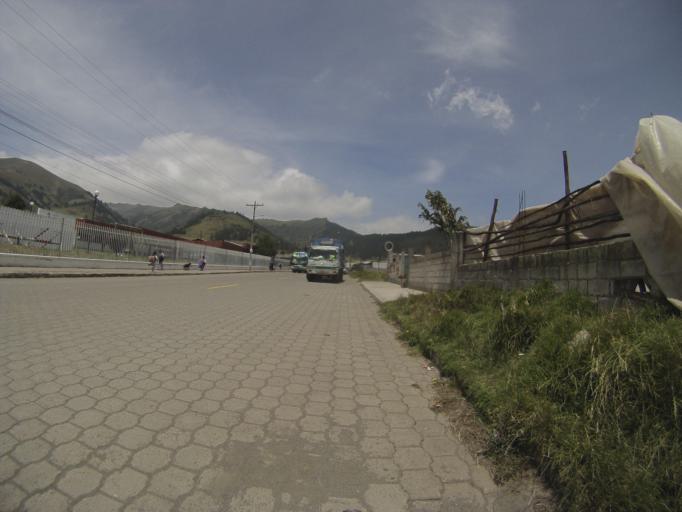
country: EC
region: Pichincha
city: Cayambe
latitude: 0.1548
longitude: -78.0657
